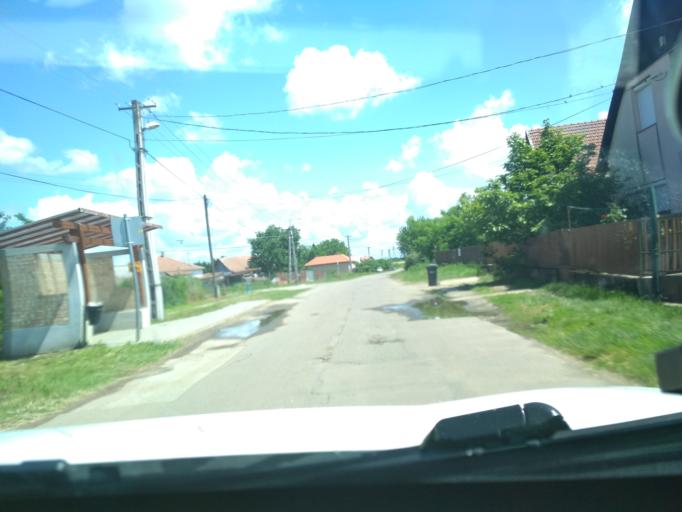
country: HU
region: Jasz-Nagykun-Szolnok
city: Abadszalok
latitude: 47.4797
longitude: 20.6141
